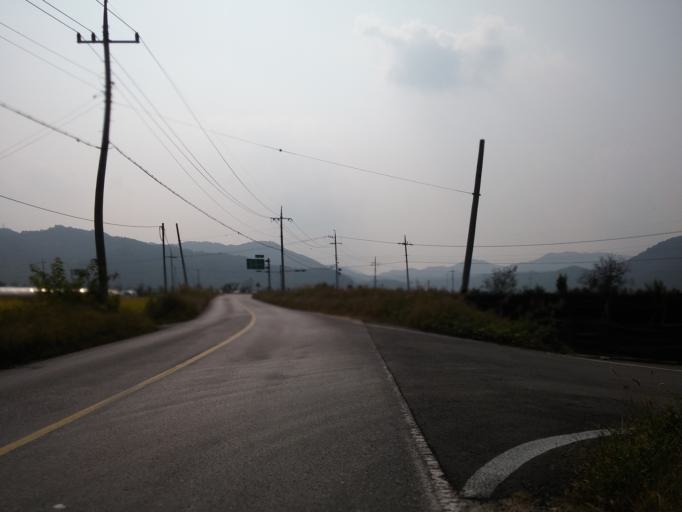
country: KR
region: Chungcheongbuk-do
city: Yong-dong
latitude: 36.3237
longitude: 127.7602
